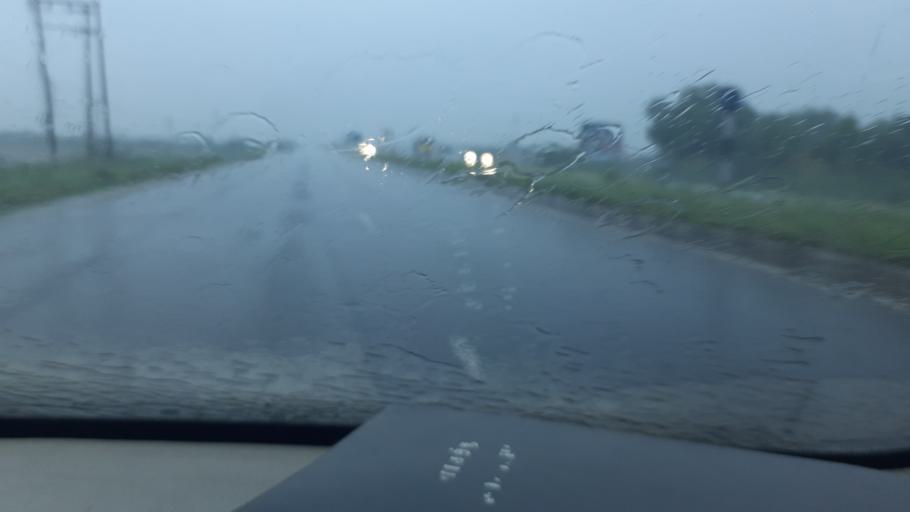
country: IN
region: Tamil Nadu
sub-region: Virudhunagar
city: Sattur
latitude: 9.4339
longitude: 77.9200
